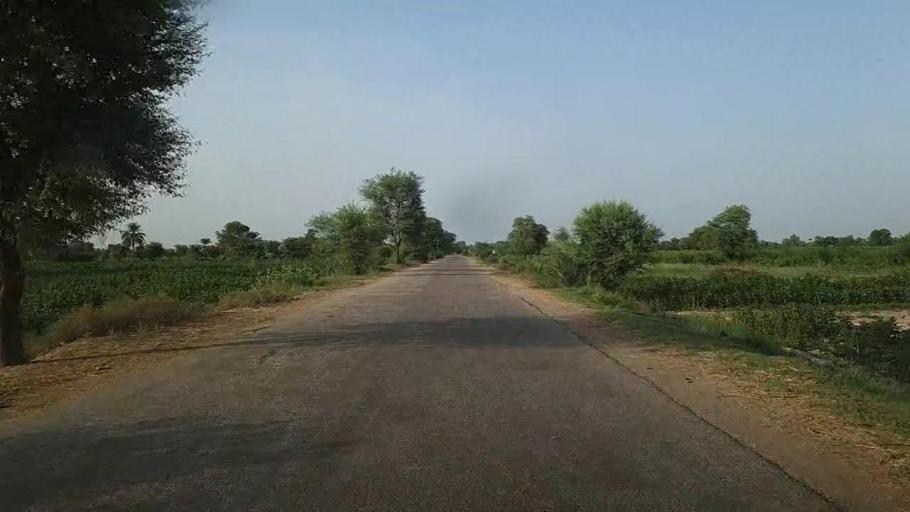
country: PK
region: Sindh
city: Ubauro
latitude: 28.1280
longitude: 69.8313
